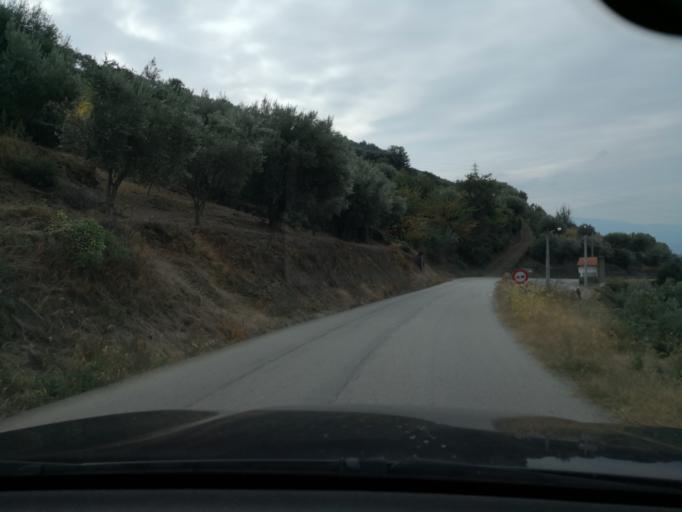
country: PT
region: Vila Real
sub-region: Peso da Regua
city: Peso da Regua
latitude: 41.1886
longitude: -7.7342
